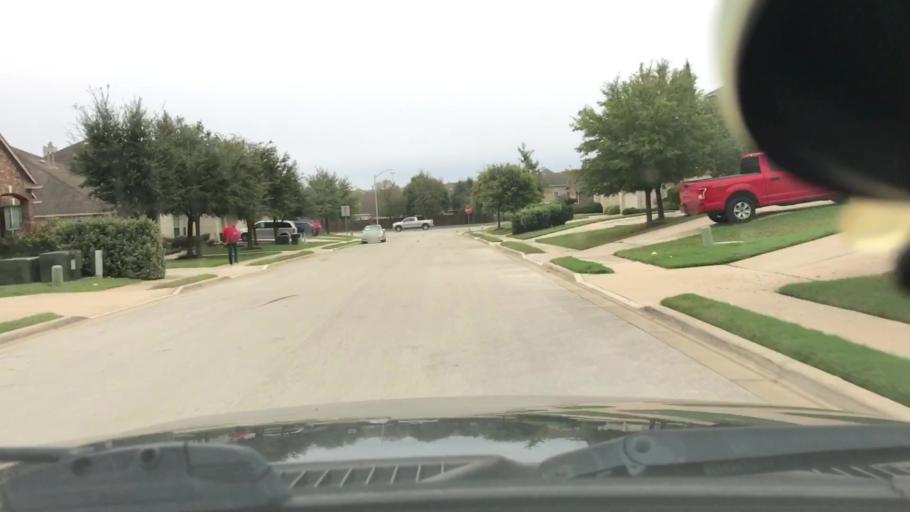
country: US
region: Texas
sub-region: Williamson County
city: Leander
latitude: 30.5415
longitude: -97.8543
